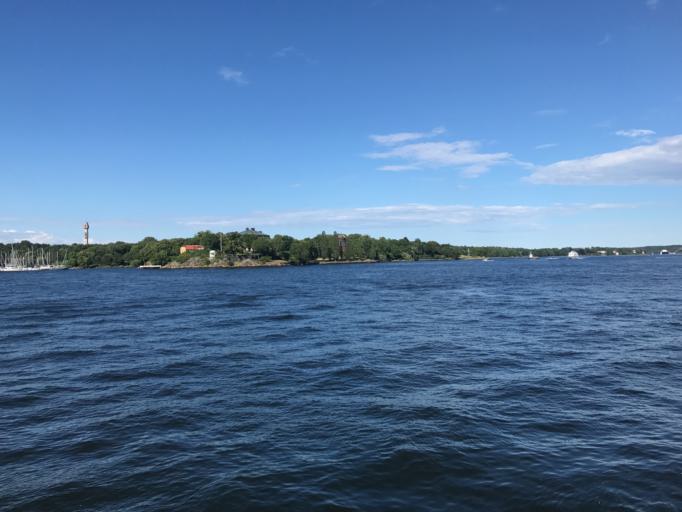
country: SE
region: Stockholm
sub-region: Stockholms Kommun
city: OEstermalm
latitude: 59.3169
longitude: 18.1080
